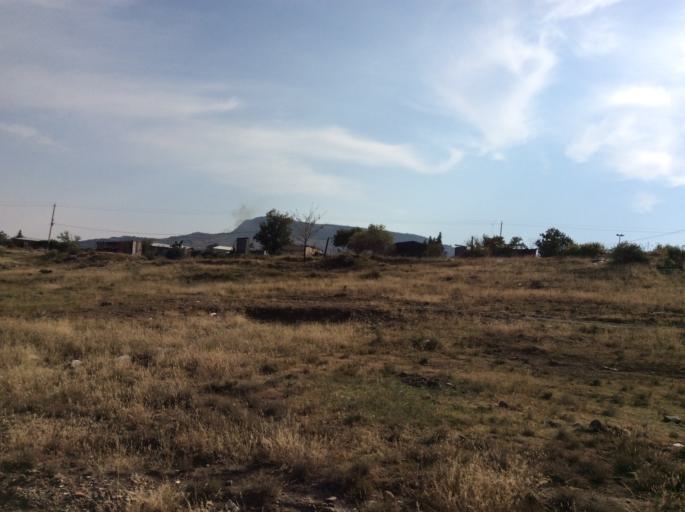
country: LS
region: Mafeteng
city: Mafeteng
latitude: -29.7250
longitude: 27.0287
